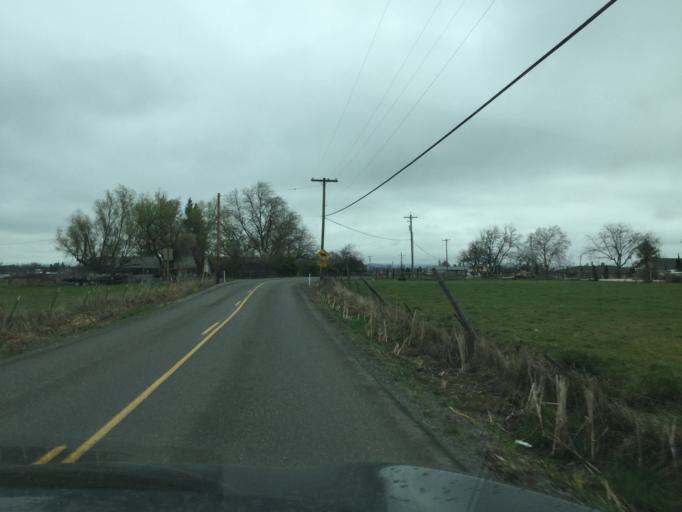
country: US
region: Oregon
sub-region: Jackson County
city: Central Point
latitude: 42.3903
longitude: -122.9540
